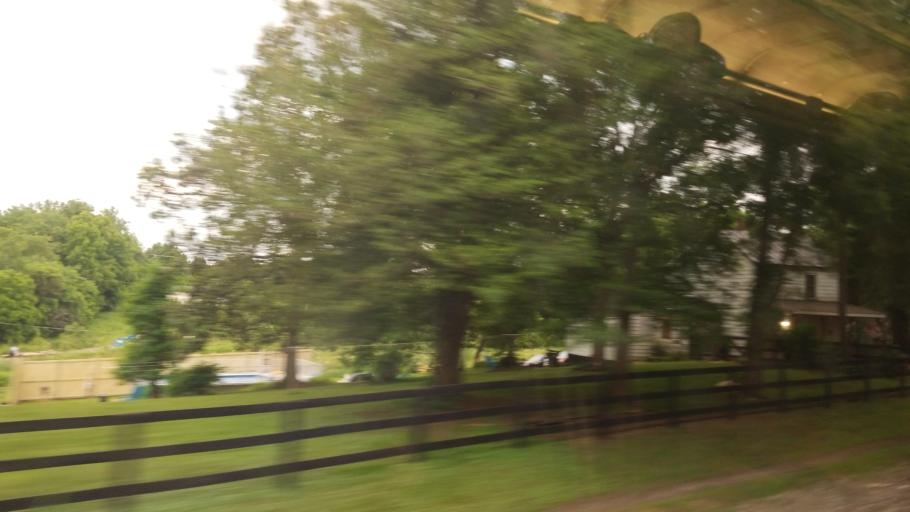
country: US
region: Virginia
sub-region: Culpeper County
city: Culpeper
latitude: 38.4688
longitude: -77.9944
